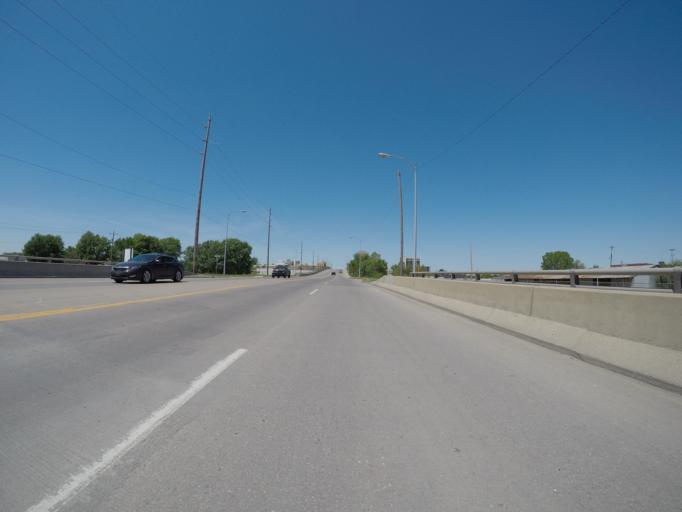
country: US
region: Kansas
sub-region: Shawnee County
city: Topeka
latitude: 39.0489
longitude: -95.6620
